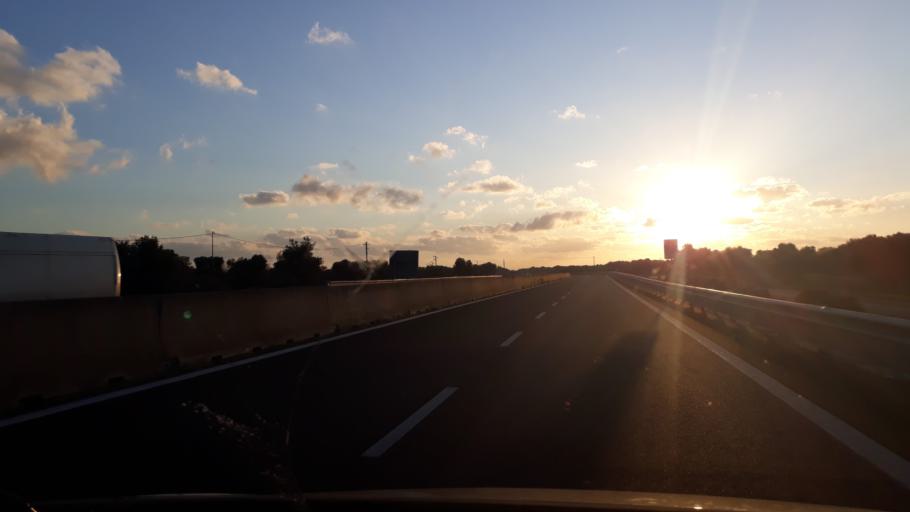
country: IT
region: Apulia
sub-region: Provincia di Brindisi
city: Ostuni
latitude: 40.7692
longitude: 17.6242
